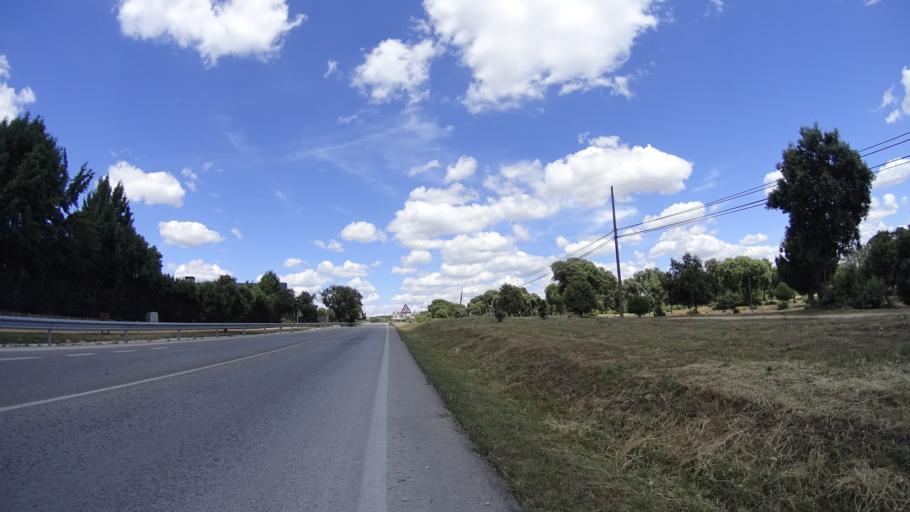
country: ES
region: Madrid
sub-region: Provincia de Madrid
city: Boadilla del Monte
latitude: 40.4150
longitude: -3.8808
